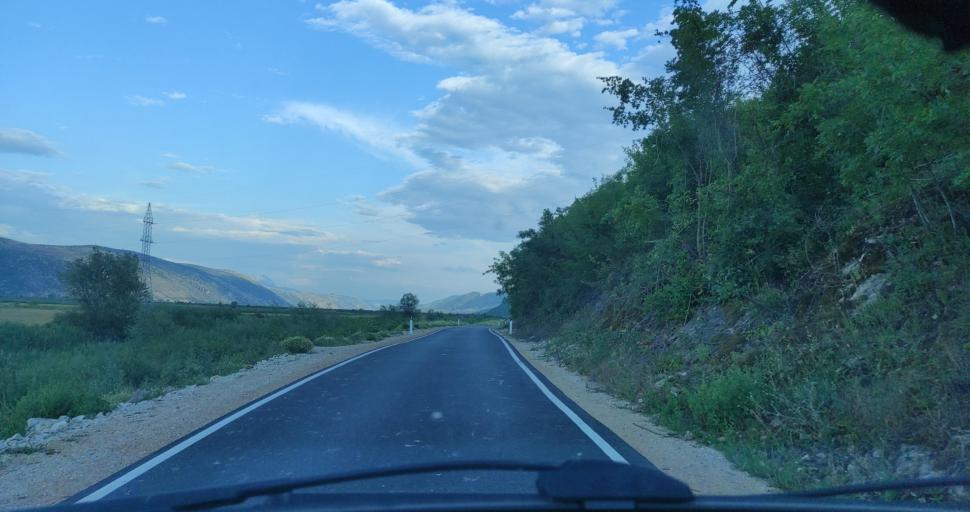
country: AL
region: Shkoder
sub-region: Rrethi i Shkodres
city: Velipoje
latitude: 41.9278
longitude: 19.4465
